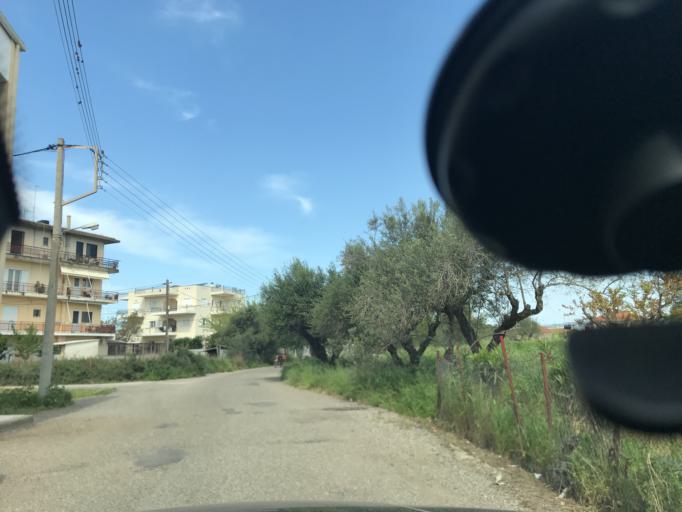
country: GR
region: West Greece
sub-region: Nomos Ileias
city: Pyrgos
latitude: 37.6792
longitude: 21.4386
